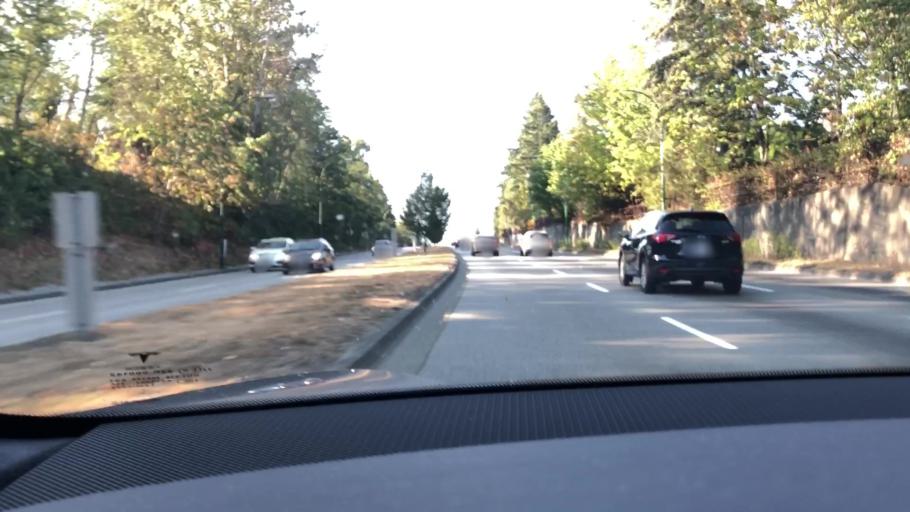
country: CA
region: British Columbia
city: Burnaby
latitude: 49.2122
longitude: -123.0236
